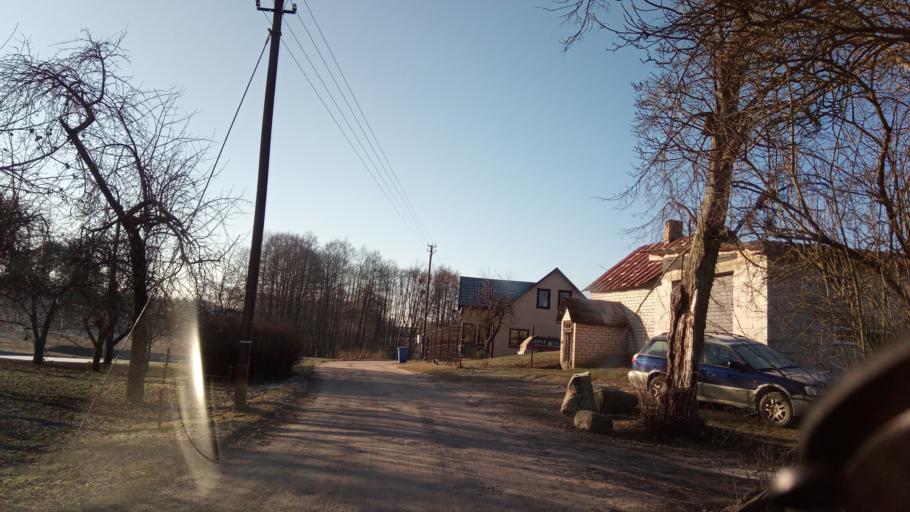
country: LT
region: Alytaus apskritis
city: Druskininkai
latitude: 54.1002
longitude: 24.0139
